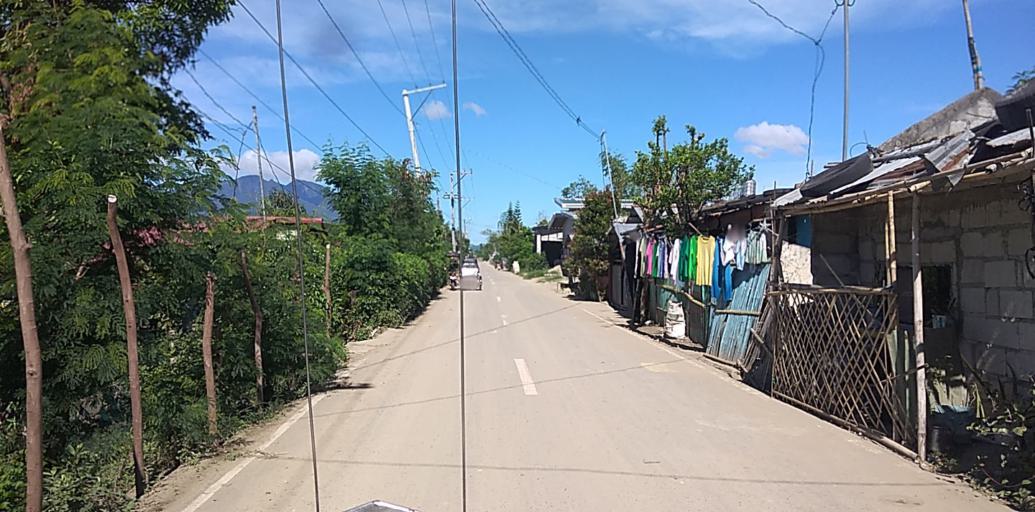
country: PH
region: Central Luzon
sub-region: Province of Pampanga
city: Candating
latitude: 15.1271
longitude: 120.8102
